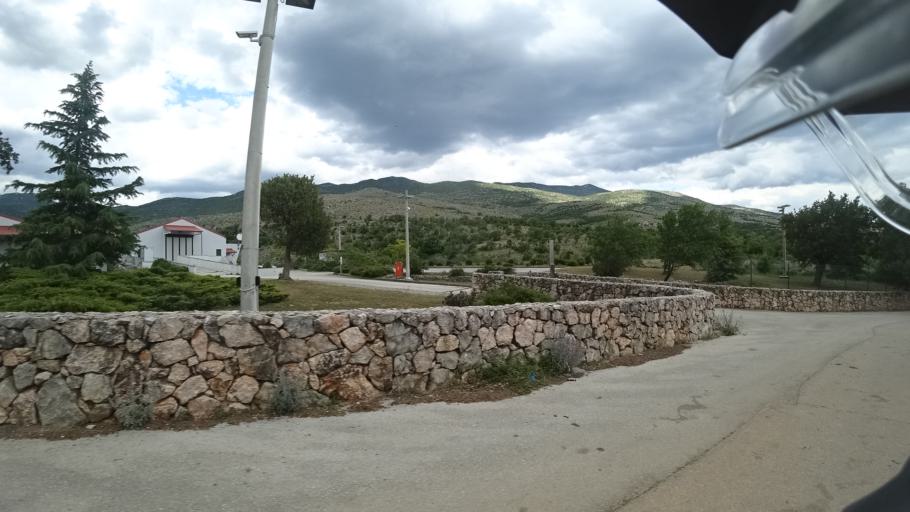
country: HR
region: Zadarska
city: Gracac
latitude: 44.1938
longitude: 15.9082
